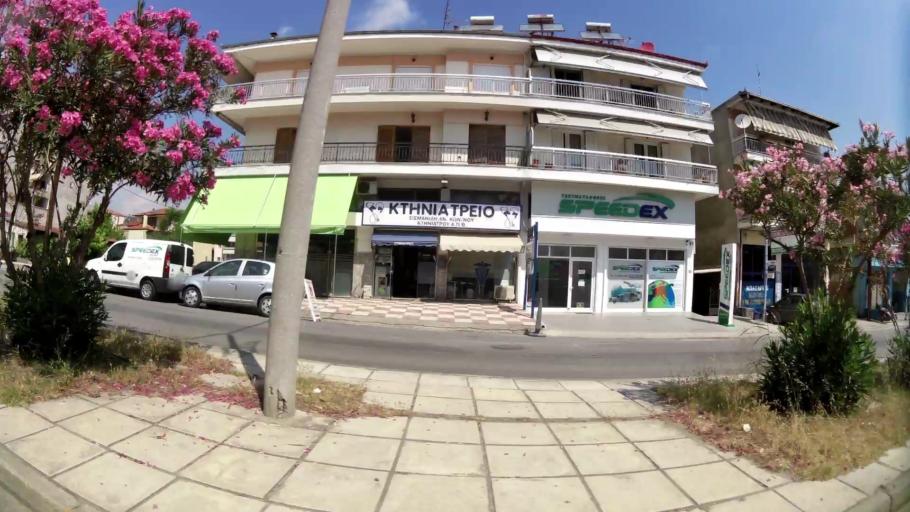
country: GR
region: Central Macedonia
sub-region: Nomos Imathias
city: Veroia
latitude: 40.5324
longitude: 22.2048
